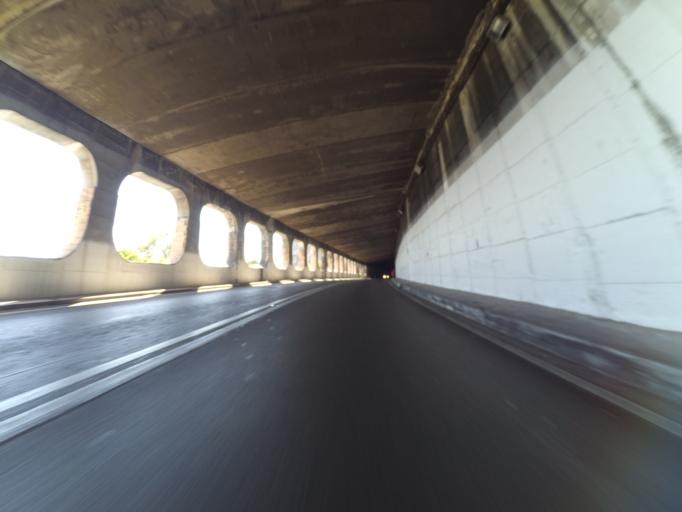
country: IT
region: Latium
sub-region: Provincia di Latina
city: Sperlonga
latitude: 41.2382
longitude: 13.4810
